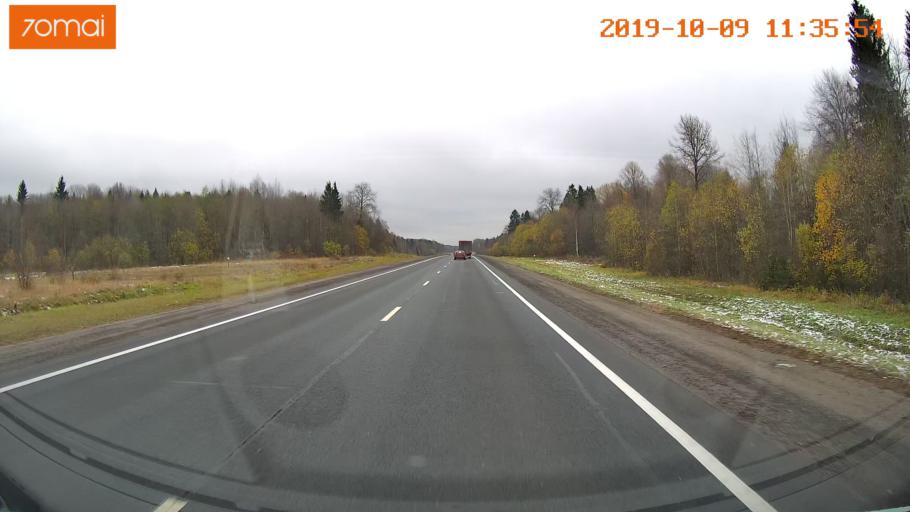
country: RU
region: Vologda
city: Gryazovets
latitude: 58.9977
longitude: 40.1308
